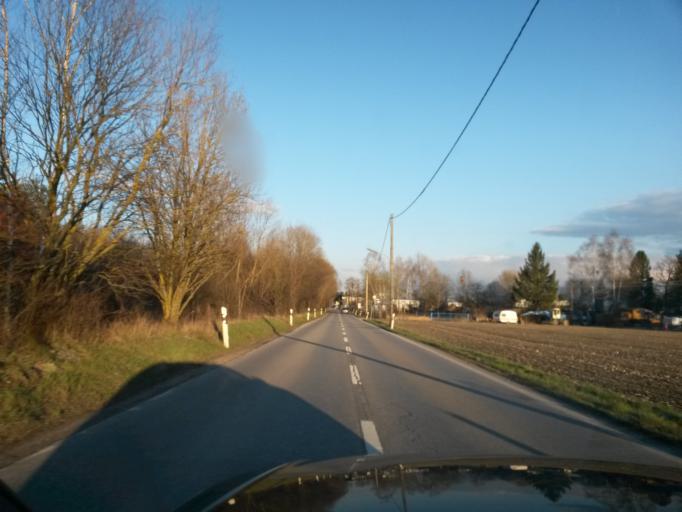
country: DE
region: Bavaria
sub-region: Upper Bavaria
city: Karlsfeld
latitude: 48.1974
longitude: 11.4791
